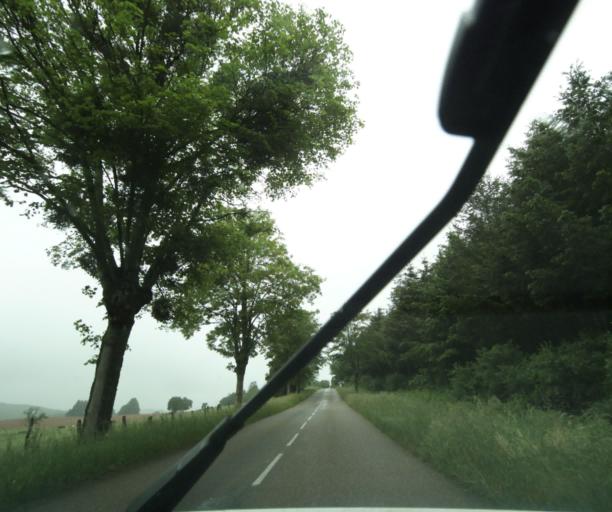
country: FR
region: Bourgogne
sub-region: Departement de Saone-et-Loire
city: Charolles
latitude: 46.4413
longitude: 4.3993
